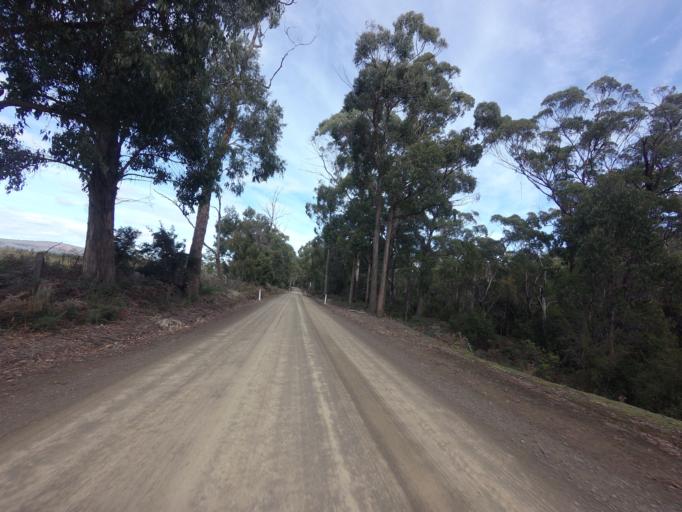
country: AU
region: Tasmania
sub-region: Clarence
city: Sandford
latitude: -43.0897
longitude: 147.7151
